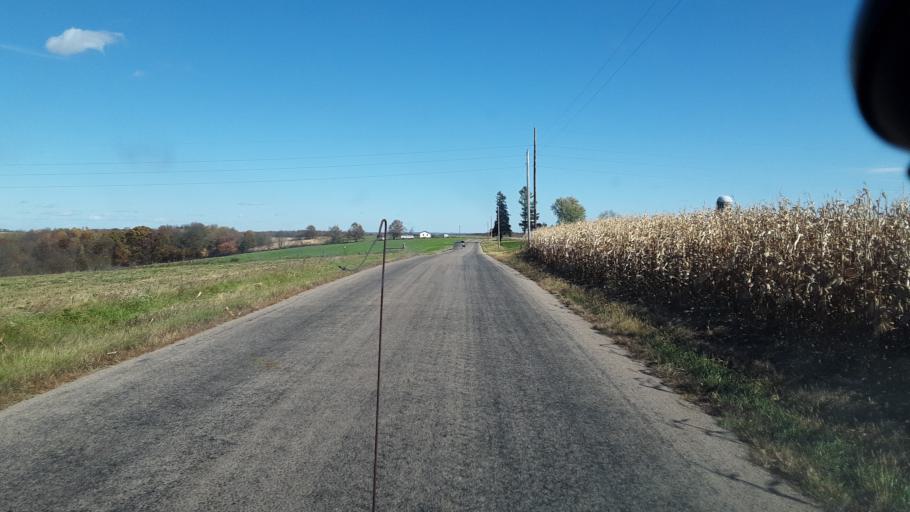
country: US
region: Wisconsin
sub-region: Vernon County
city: Hillsboro
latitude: 43.6931
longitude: -90.4390
